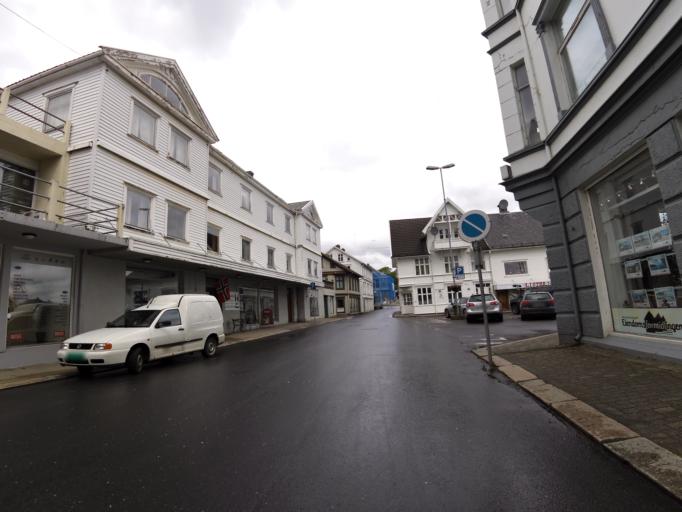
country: NO
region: Vest-Agder
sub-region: Farsund
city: Farsund
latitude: 58.0939
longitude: 6.8049
